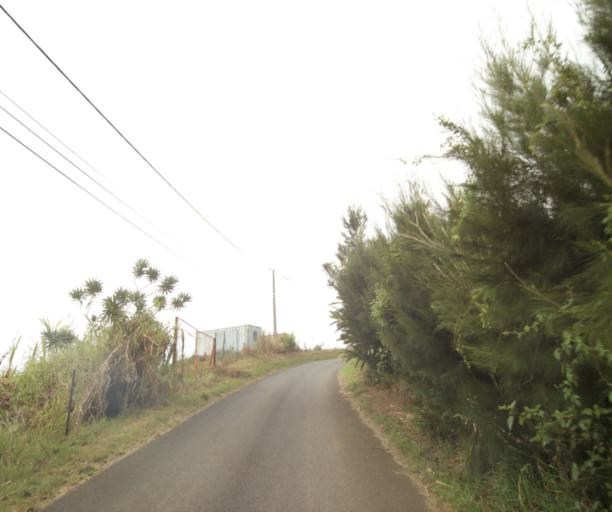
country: RE
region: Reunion
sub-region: Reunion
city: Saint-Paul
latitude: -21.0115
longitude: 55.3382
